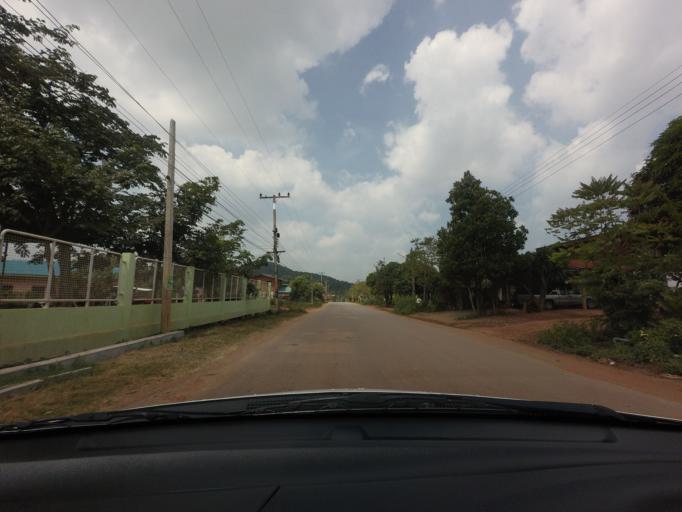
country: TH
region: Nakhon Ratchasima
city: Pak Chong
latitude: 14.5528
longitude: 101.5765
